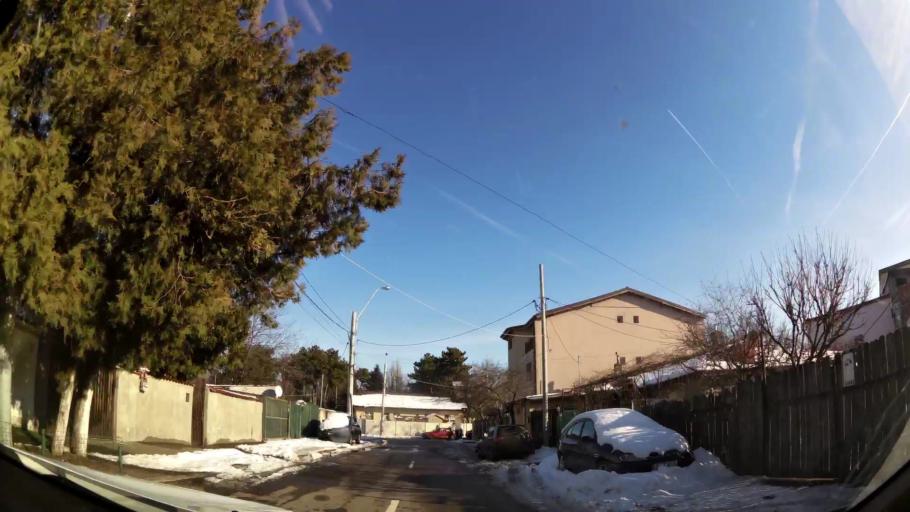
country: RO
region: Ilfov
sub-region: Voluntari City
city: Voluntari
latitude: 44.4810
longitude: 26.1531
